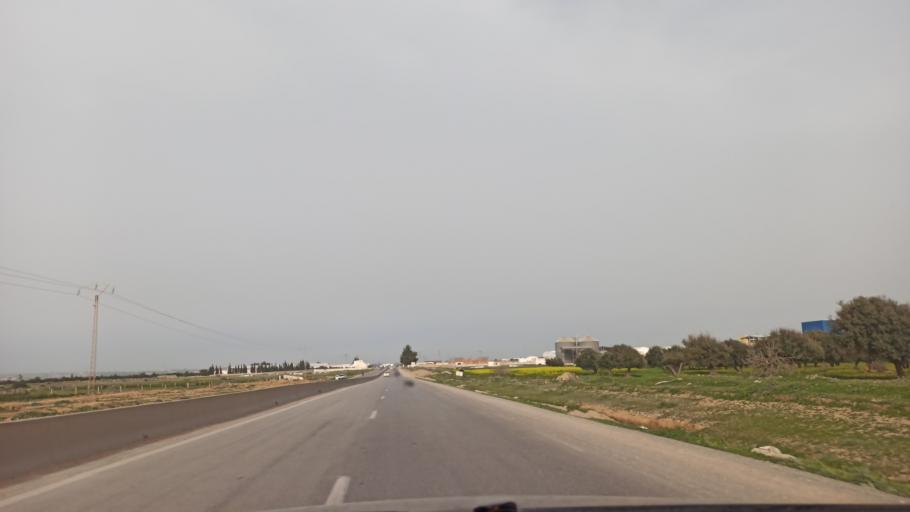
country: TN
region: Tunis
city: La Mohammedia
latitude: 36.5779
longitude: 10.0926
